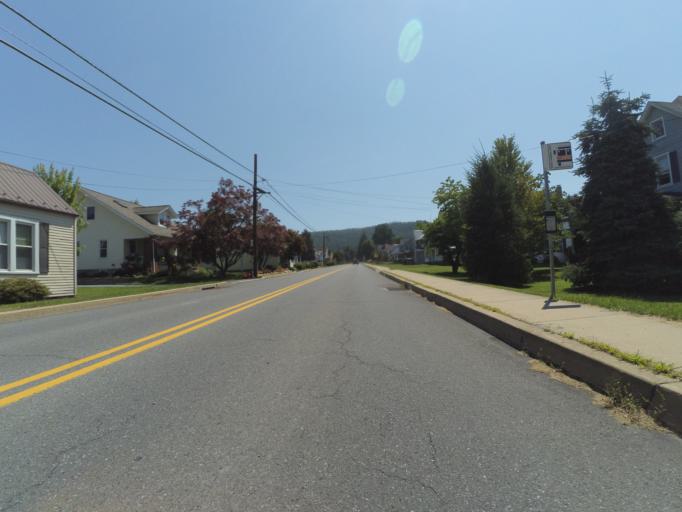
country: US
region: Pennsylvania
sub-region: Centre County
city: Pleasant Gap
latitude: 40.8675
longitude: -77.7447
